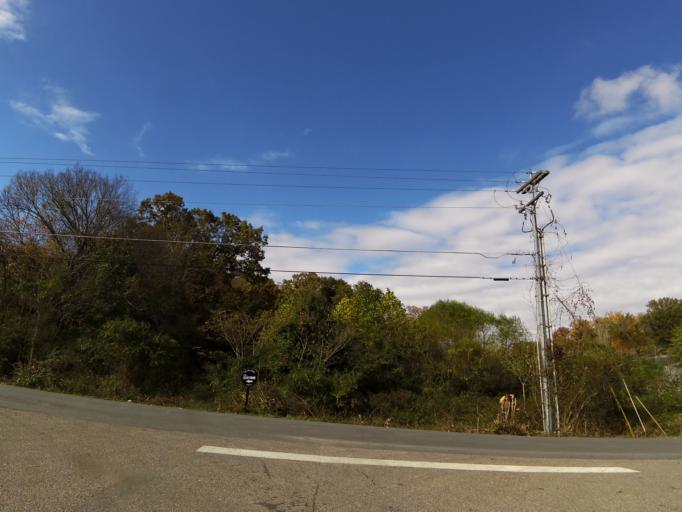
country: US
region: Tennessee
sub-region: Blount County
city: Eagleton Village
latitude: 35.8119
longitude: -83.9472
